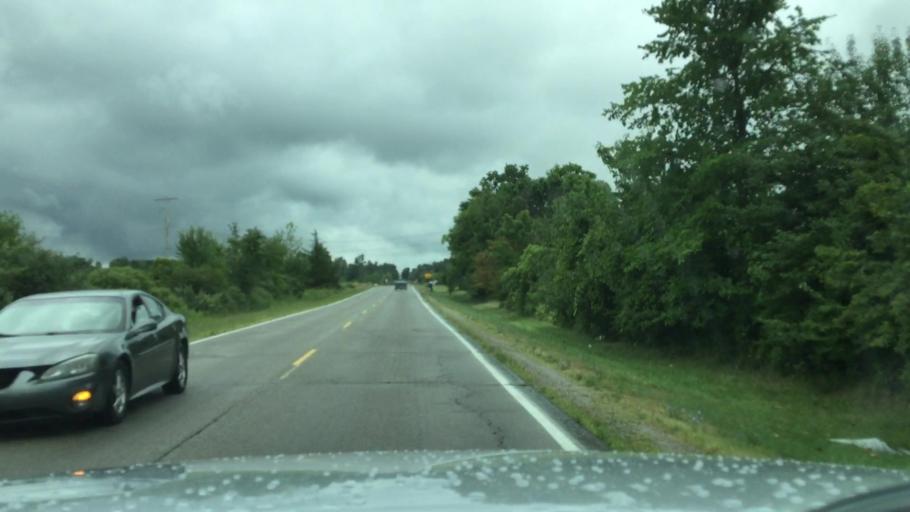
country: US
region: Michigan
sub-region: Genesee County
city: Clio
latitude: 43.1224
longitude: -83.7738
